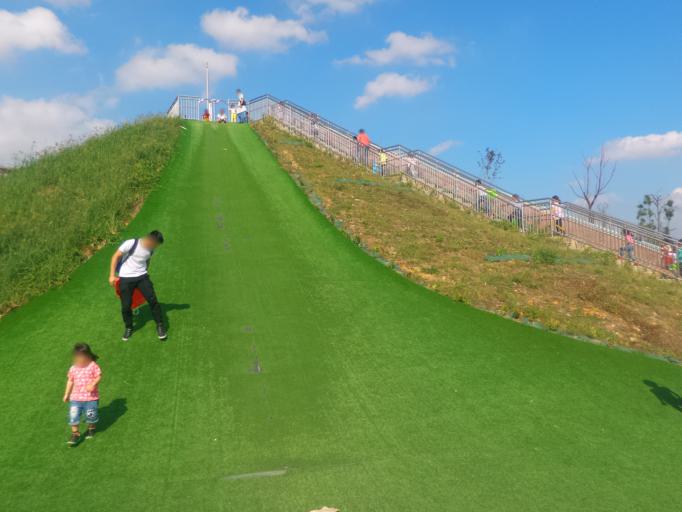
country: TW
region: Taipei
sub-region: Taipei
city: Banqiao
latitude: 25.0029
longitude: 121.4781
